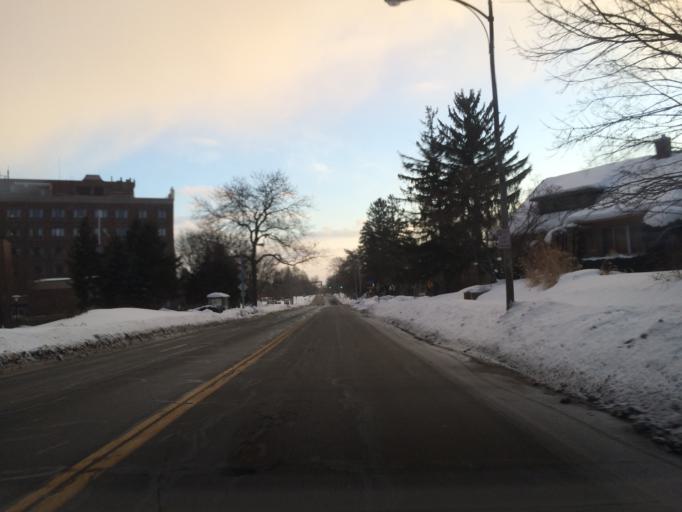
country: US
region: New York
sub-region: Monroe County
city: Rochester
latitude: 43.1316
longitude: -77.6099
